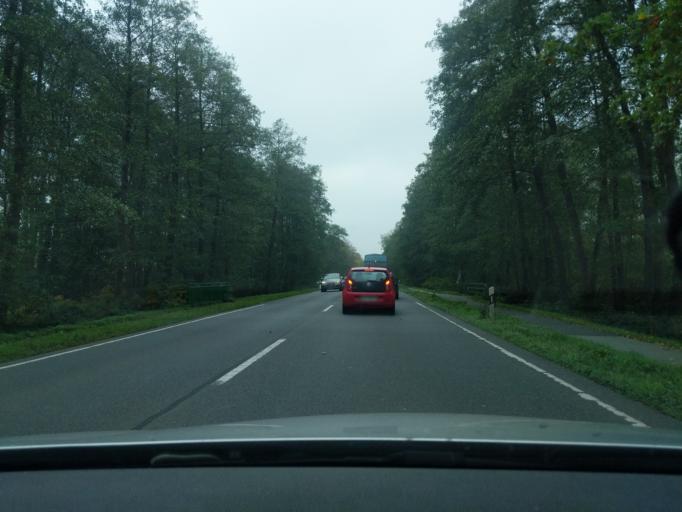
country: DE
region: Lower Saxony
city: Burweg
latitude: 53.6294
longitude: 9.2611
